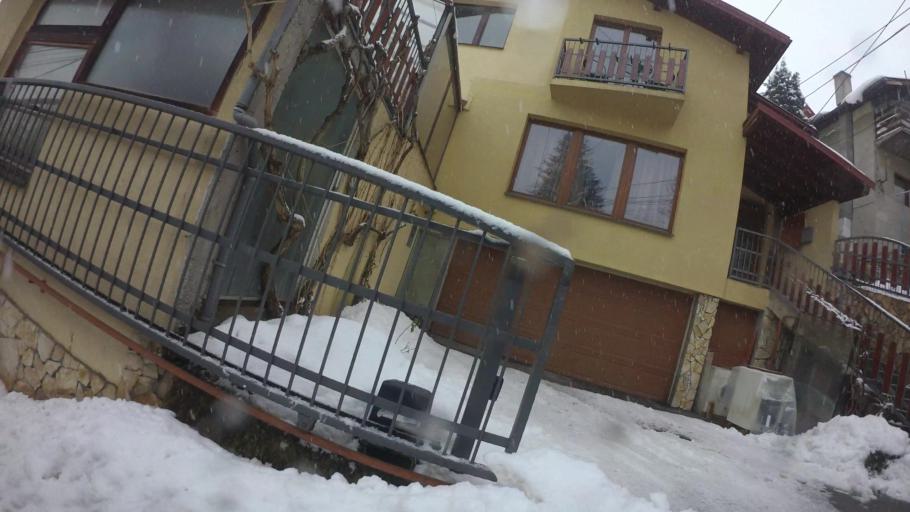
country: BA
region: Federation of Bosnia and Herzegovina
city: Kobilja Glava
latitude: 43.8509
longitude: 18.4373
